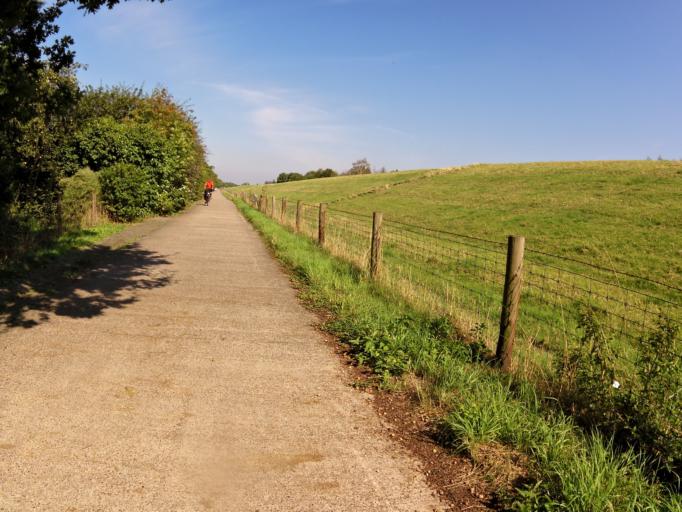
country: DE
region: Lower Saxony
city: Elsfleth
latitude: 53.2722
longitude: 8.4805
